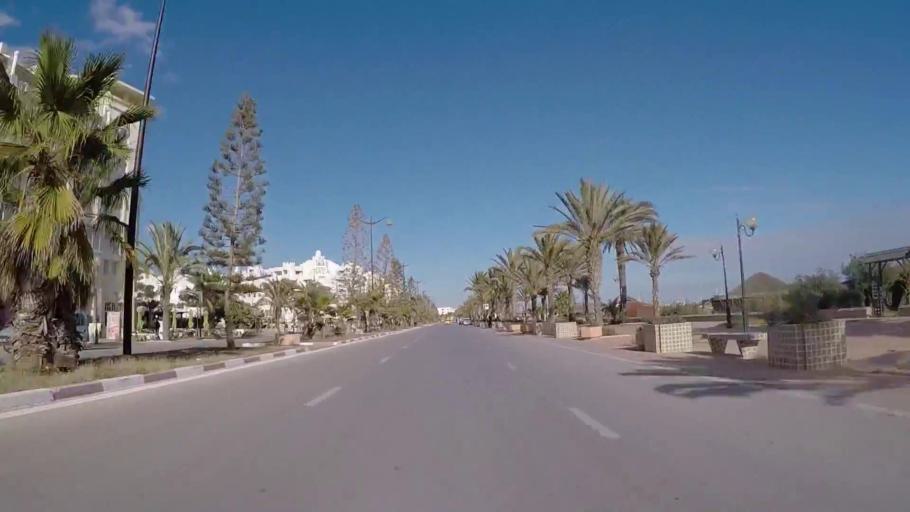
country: TN
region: Nabul
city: Al Hammamat
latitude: 36.3676
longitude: 10.5391
